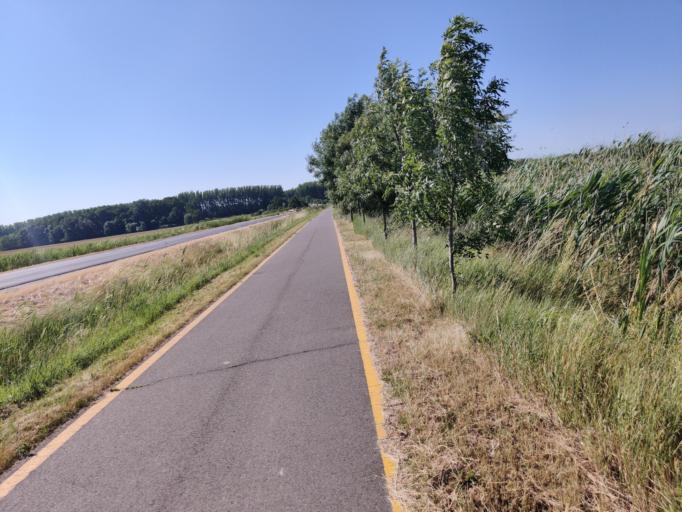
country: HU
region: Hajdu-Bihar
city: Balmazujvaros
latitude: 47.5875
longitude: 21.3448
